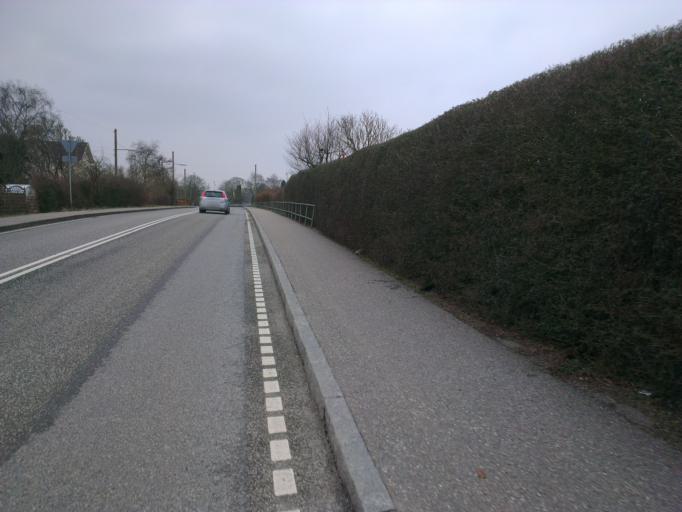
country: DK
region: Capital Region
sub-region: Frederikssund Kommune
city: Slangerup
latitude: 55.8534
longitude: 12.1695
